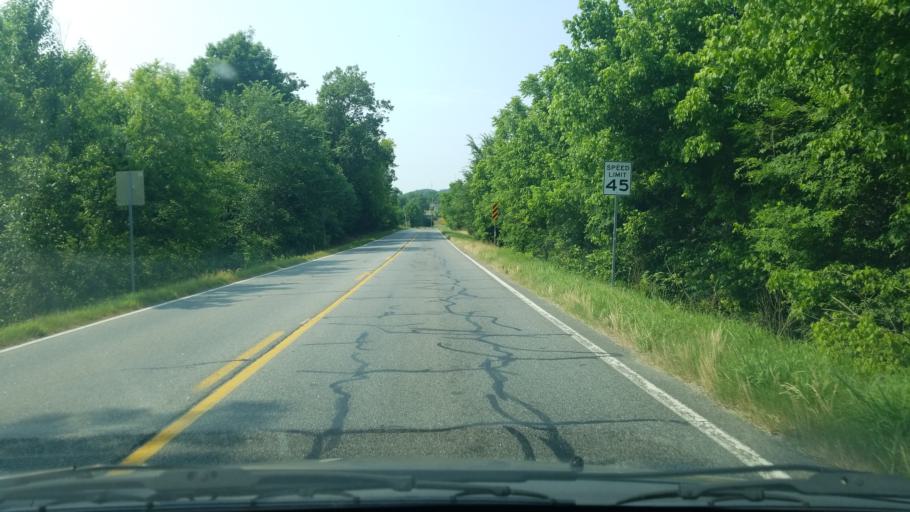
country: US
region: Georgia
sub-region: Catoosa County
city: Ringgold
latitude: 34.9305
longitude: -85.1038
